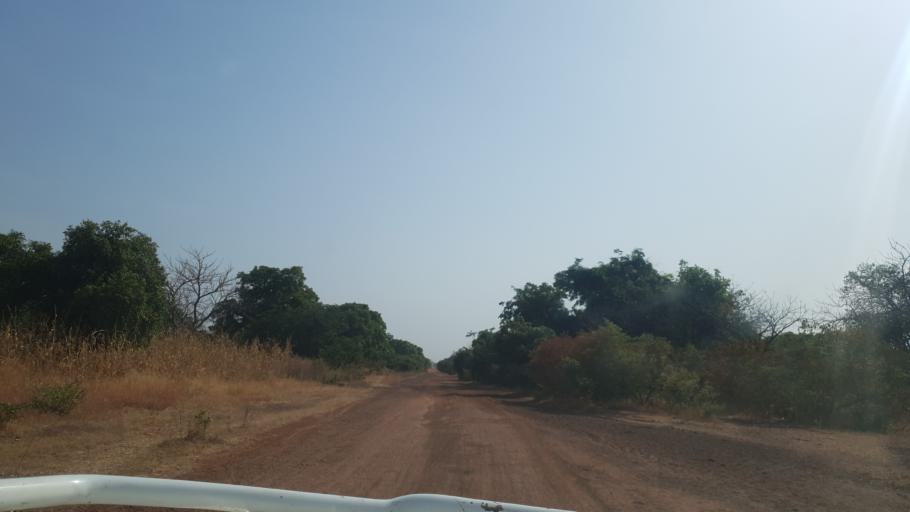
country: ML
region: Koulikoro
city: Dioila
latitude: 12.6683
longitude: -6.6848
